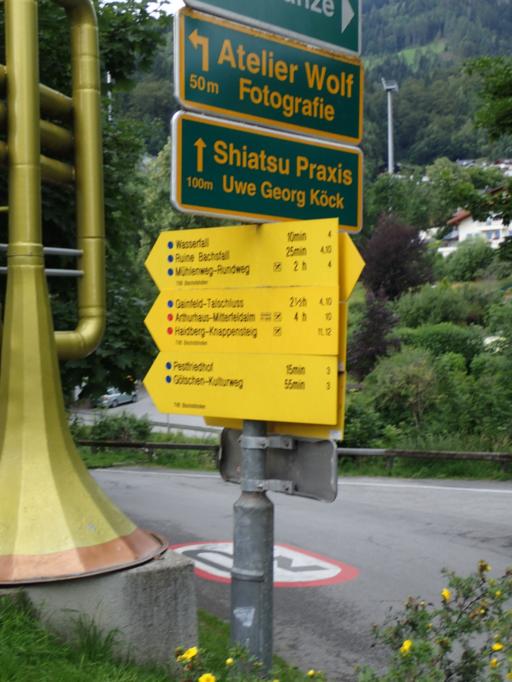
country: AT
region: Salzburg
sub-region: Politischer Bezirk Sankt Johann im Pongau
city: Bischofshofen
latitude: 47.4142
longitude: 13.2115
